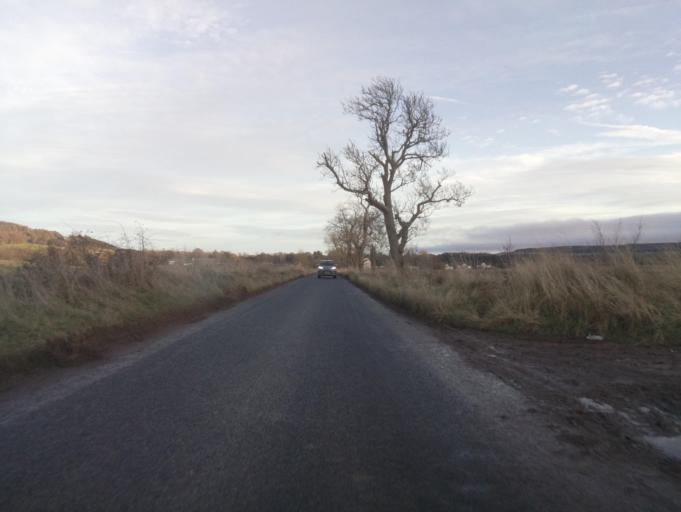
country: GB
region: Scotland
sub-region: Angus
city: Forfar
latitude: 56.5866
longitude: -2.9037
